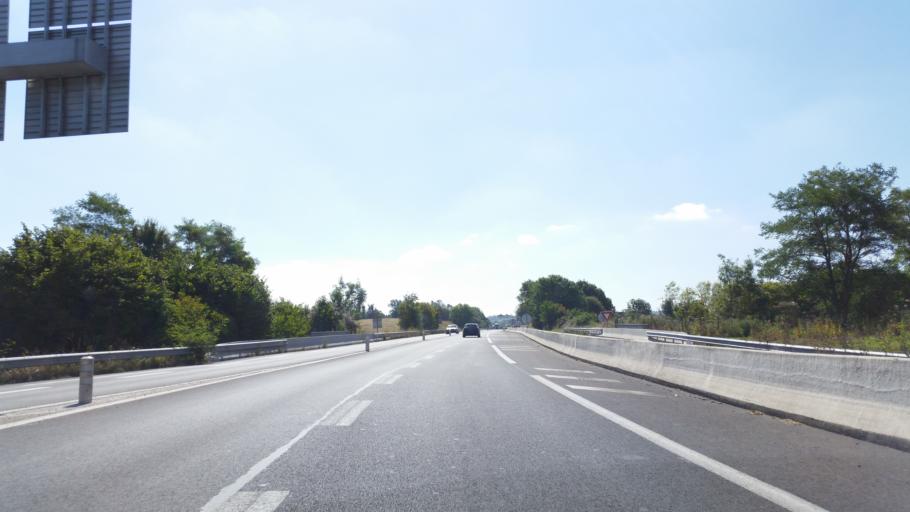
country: FR
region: Lower Normandy
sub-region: Departement du Calvados
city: Saint-Gatien-des-Bois
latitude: 49.2893
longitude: 0.2042
